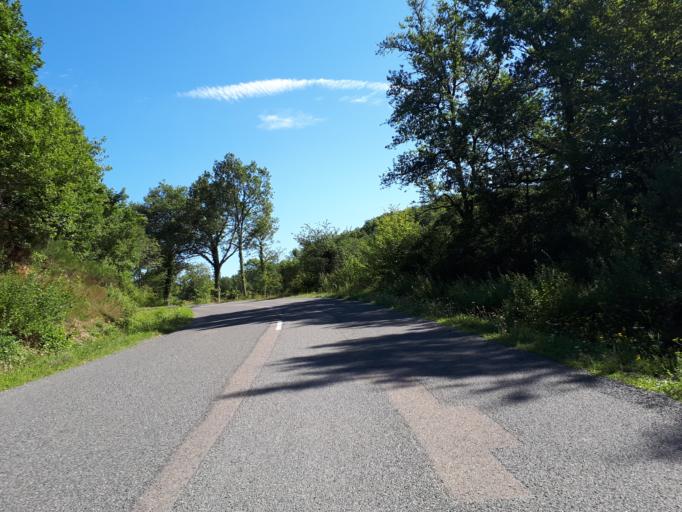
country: FR
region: Rhone-Alpes
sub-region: Departement de la Loire
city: Bussieres
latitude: 45.8233
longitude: 4.2519
